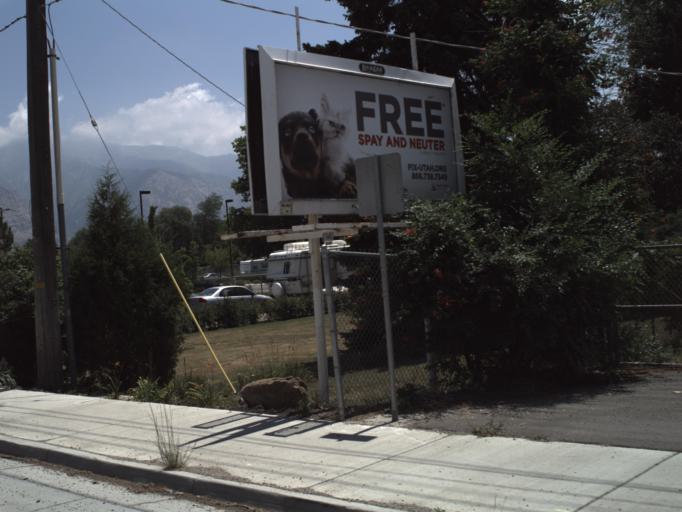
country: US
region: Utah
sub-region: Weber County
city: Ogden
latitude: 41.2444
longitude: -111.9920
